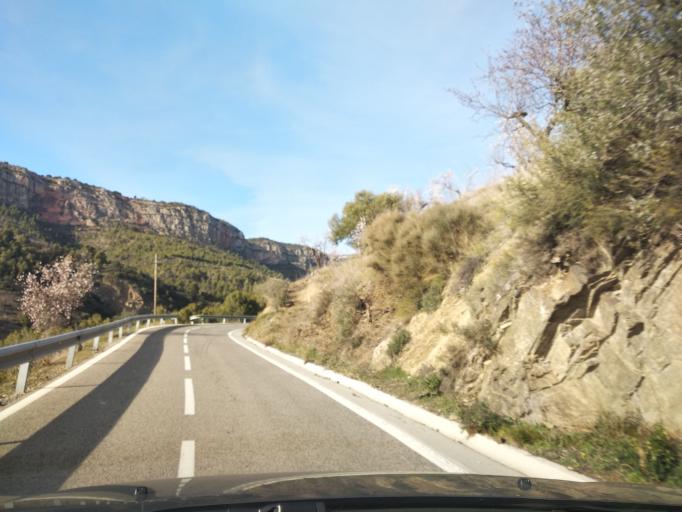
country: ES
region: Catalonia
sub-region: Provincia de Tarragona
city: Margalef
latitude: 41.2328
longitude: 0.7812
